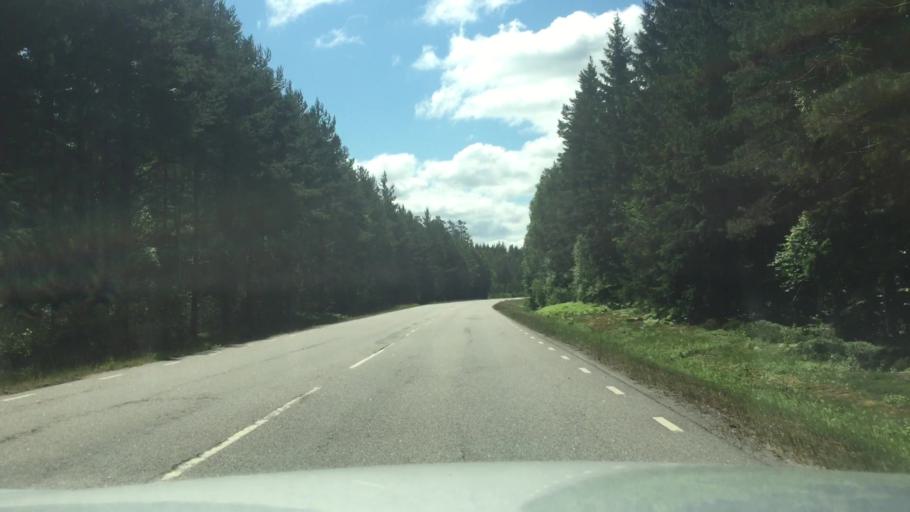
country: SE
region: Vaestra Goetaland
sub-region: Karlsborgs Kommun
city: Molltorp
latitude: 58.6177
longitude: 14.3891
